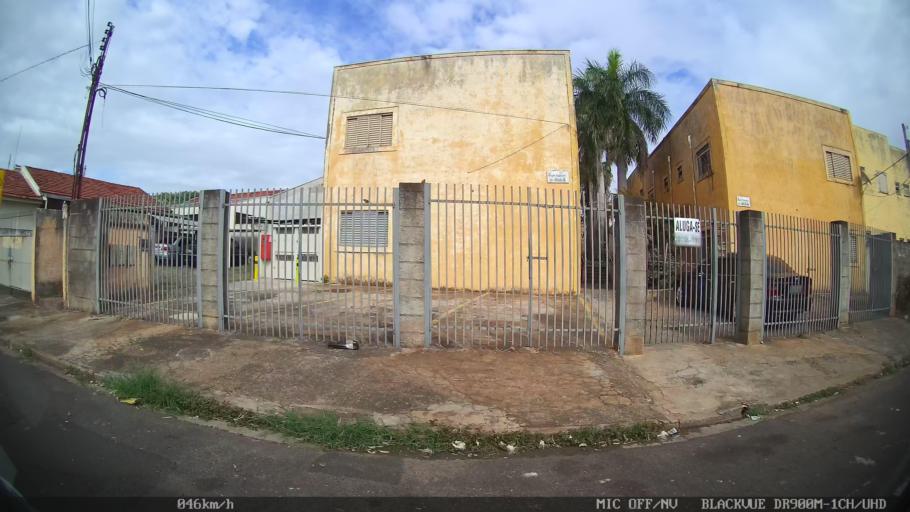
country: BR
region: Sao Paulo
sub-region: Sao Jose Do Rio Preto
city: Sao Jose do Rio Preto
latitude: -20.8163
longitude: -49.3511
